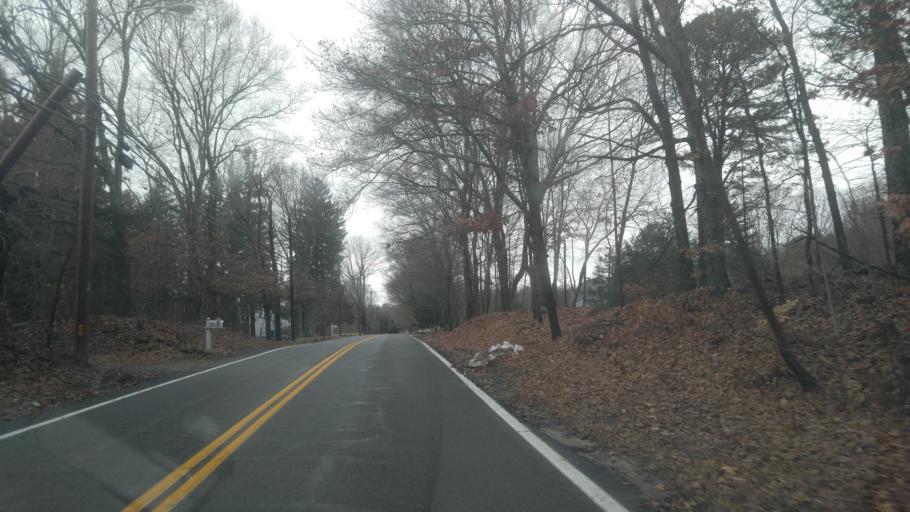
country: US
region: Rhode Island
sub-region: Kent County
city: West Warwick
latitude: 41.6562
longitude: -71.5337
